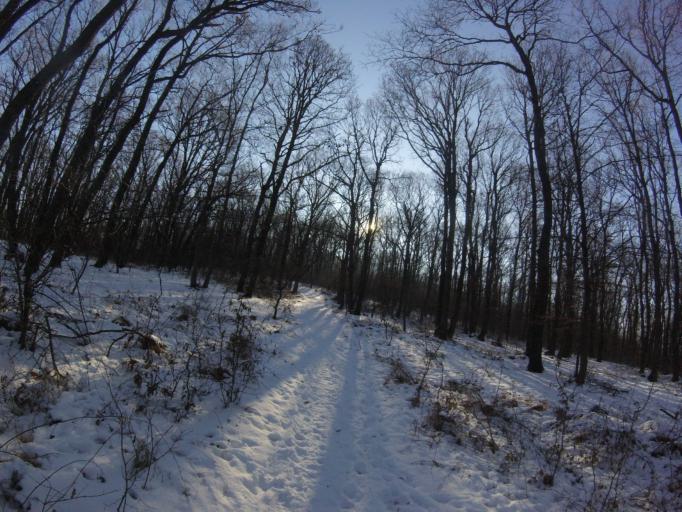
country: SK
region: Nitriansky
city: Sahy
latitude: 47.9902
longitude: 18.8878
